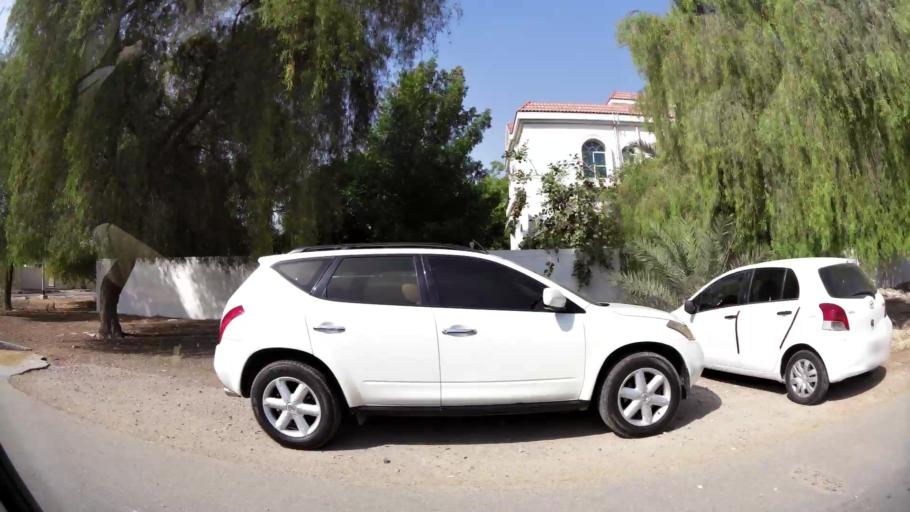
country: AE
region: Ash Shariqah
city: Sharjah
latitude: 25.2711
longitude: 55.4018
